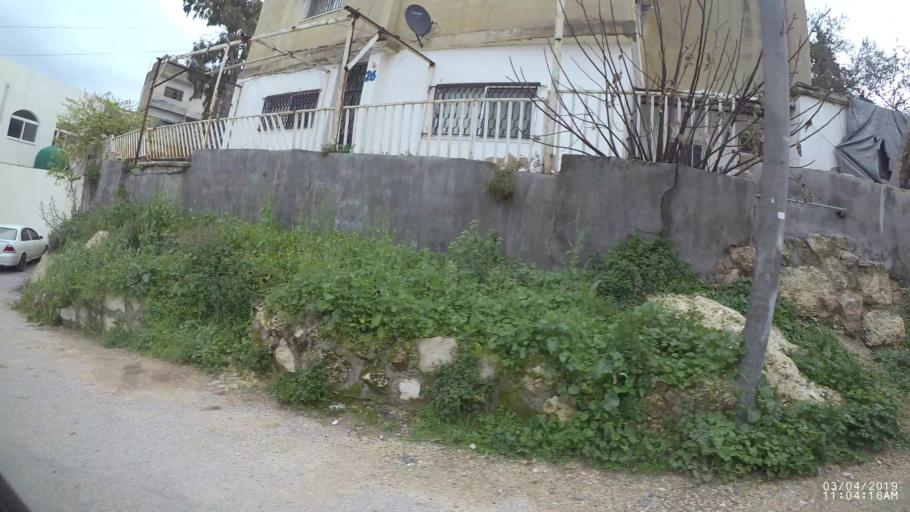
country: JO
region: Amman
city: Wadi as Sir
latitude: 31.9483
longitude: 35.8152
